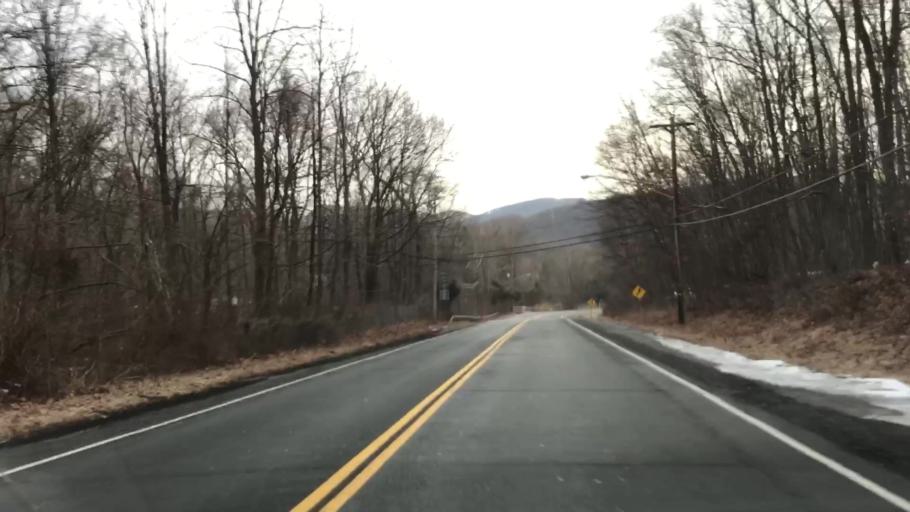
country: US
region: New York
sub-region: Rockland County
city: Thiells
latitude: 41.2376
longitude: -74.0293
